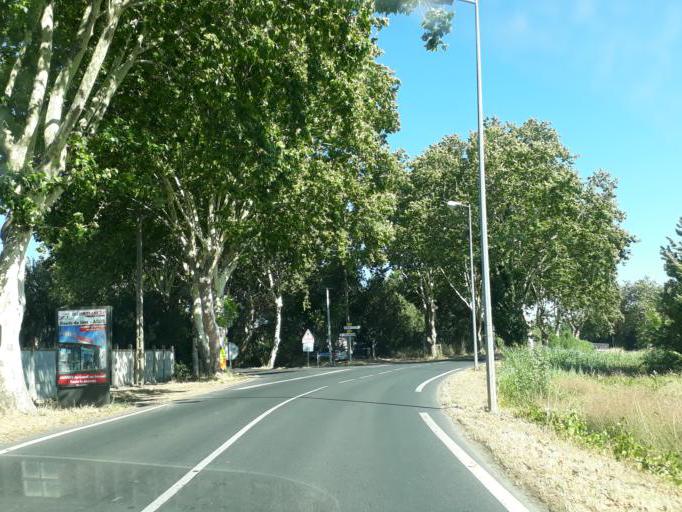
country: FR
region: Languedoc-Roussillon
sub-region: Departement de l'Herault
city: Florensac
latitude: 43.3795
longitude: 3.4698
